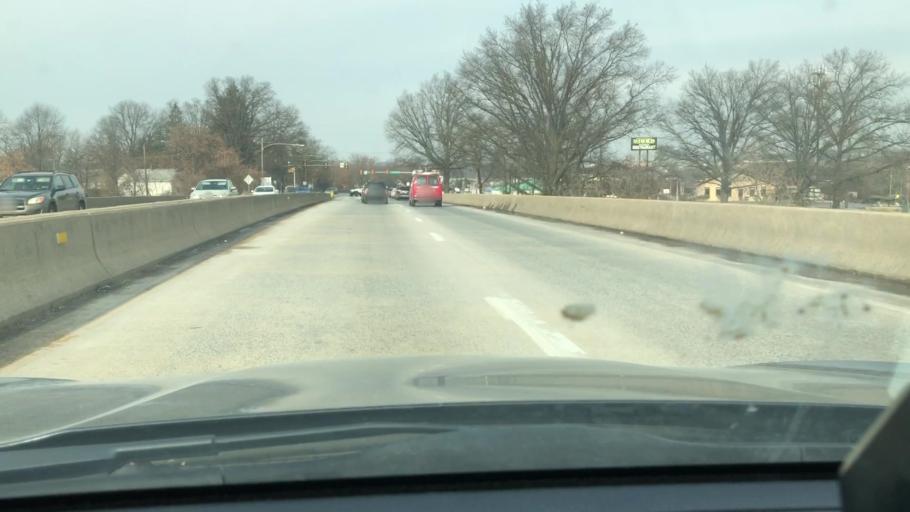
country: US
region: Pennsylvania
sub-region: Montgomery County
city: Pottstown
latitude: 40.2474
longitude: -75.6609
